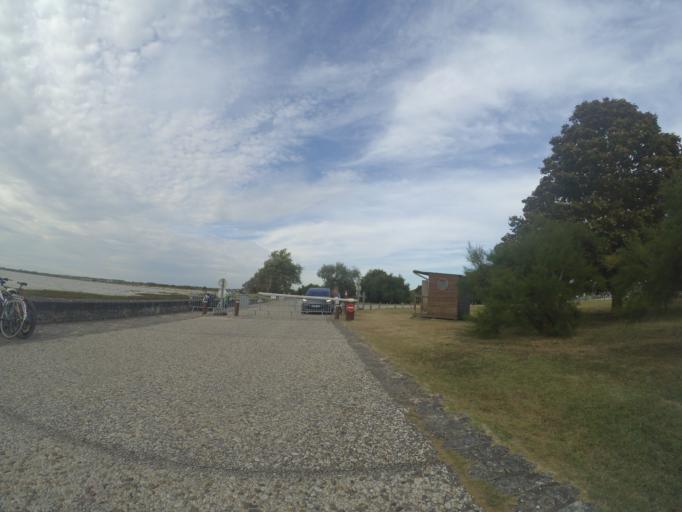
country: FR
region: Poitou-Charentes
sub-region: Departement de la Charente-Maritime
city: Meschers-sur-Gironde
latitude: 45.5360
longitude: -0.9069
